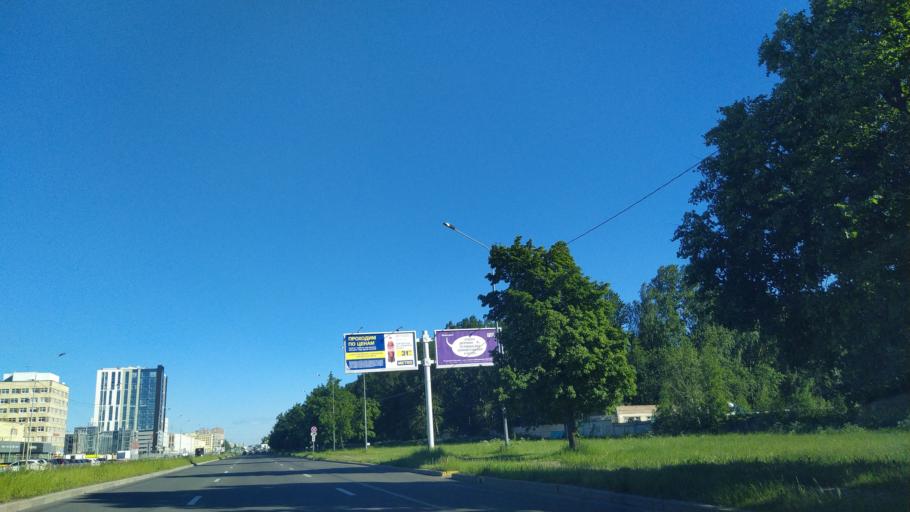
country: RU
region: St.-Petersburg
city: Kupchino
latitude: 59.8878
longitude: 30.3825
